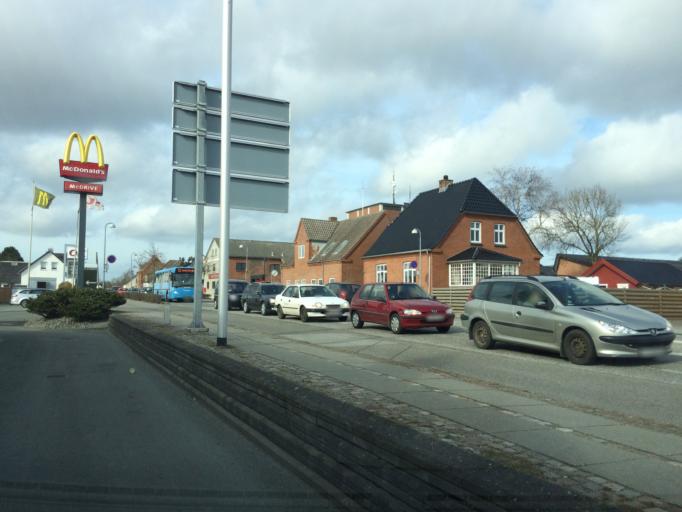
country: DK
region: Central Jutland
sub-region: Norddjurs Kommune
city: Grenaa
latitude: 56.4058
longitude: 10.8737
